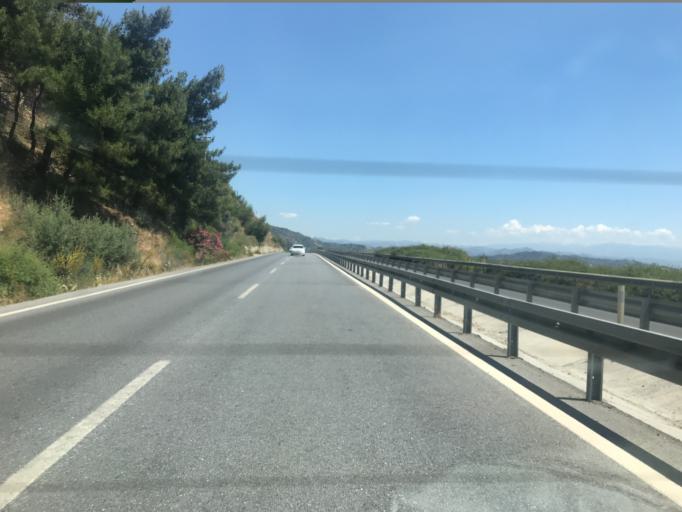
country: TR
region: Aydin
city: Ortaklar
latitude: 37.8056
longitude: 27.4778
